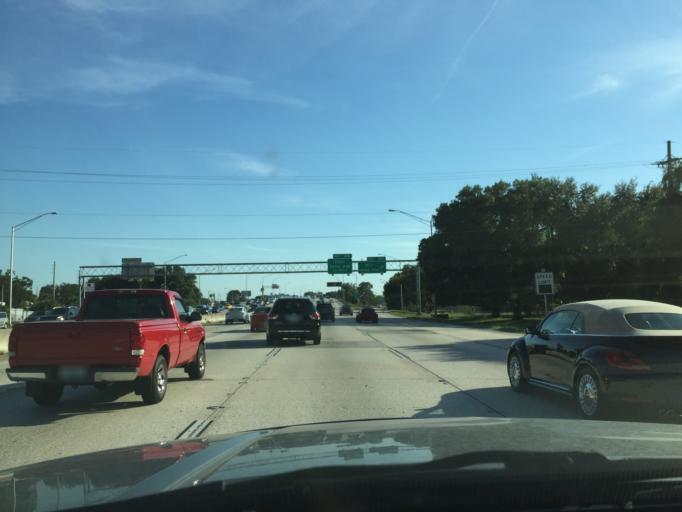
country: US
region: Florida
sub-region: Orange County
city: Orlando
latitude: 28.5243
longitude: -81.3864
